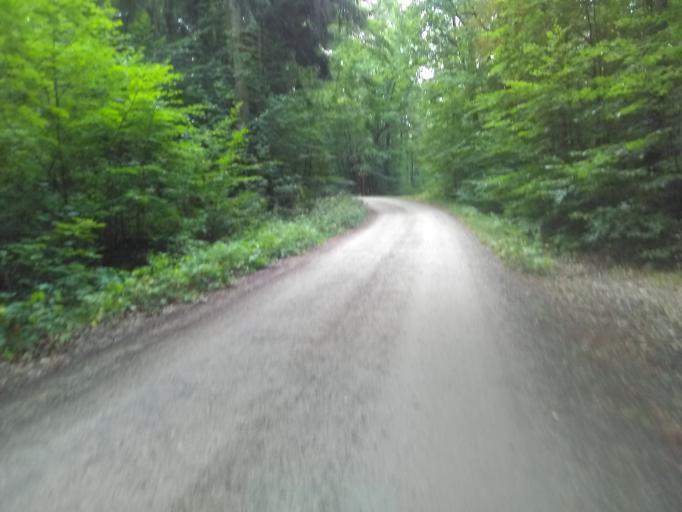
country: DE
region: Bavaria
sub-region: Upper Franconia
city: Bamberg
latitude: 49.8634
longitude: 10.8989
